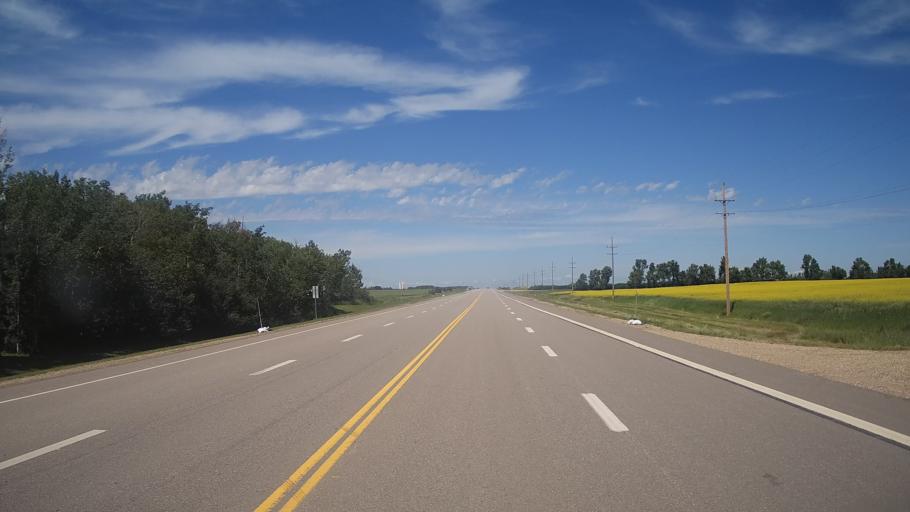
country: CA
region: Saskatchewan
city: Langenburg
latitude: 50.6303
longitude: -101.2768
